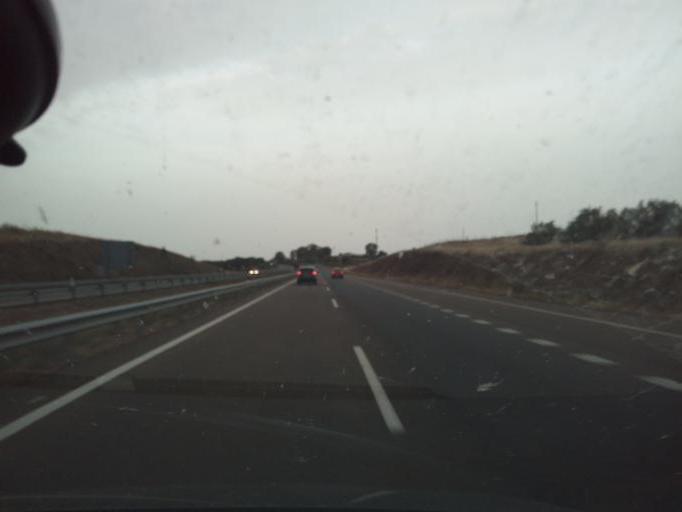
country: ES
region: Extremadura
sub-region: Provincia de Badajoz
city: San Pedro de Merida
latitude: 38.9484
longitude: -6.1937
